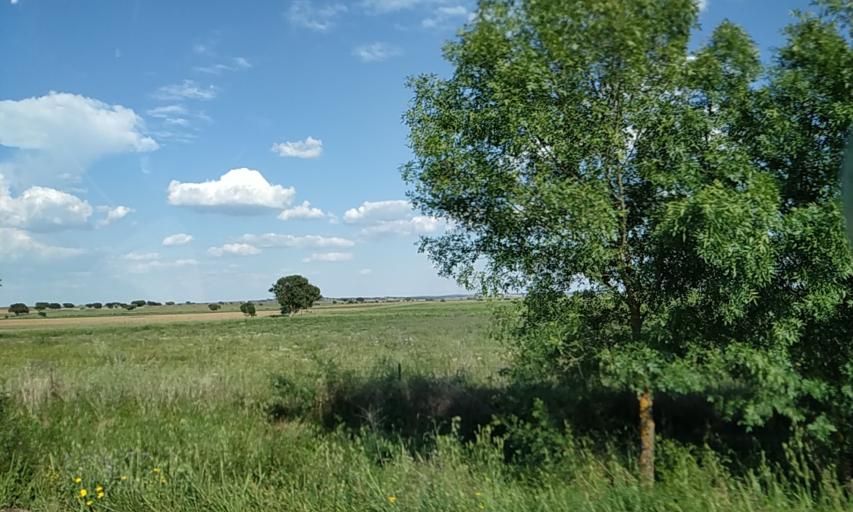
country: PT
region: Evora
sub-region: Estremoz
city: Estremoz
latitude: 38.9747
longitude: -7.4886
